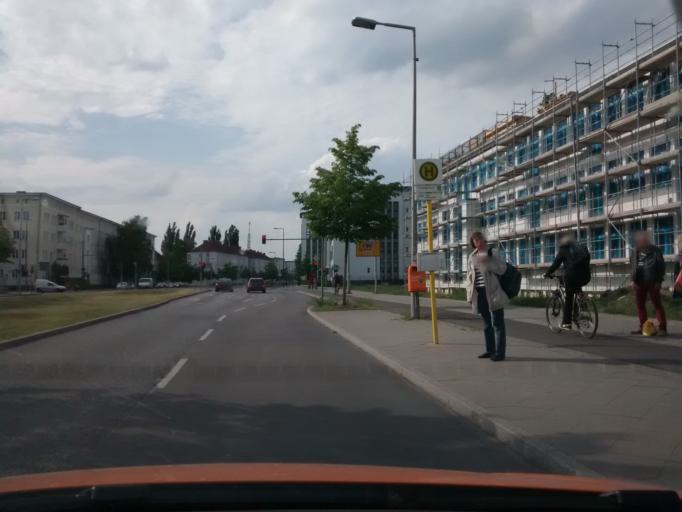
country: DE
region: Berlin
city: Johannisthal
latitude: 52.4459
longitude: 13.5154
